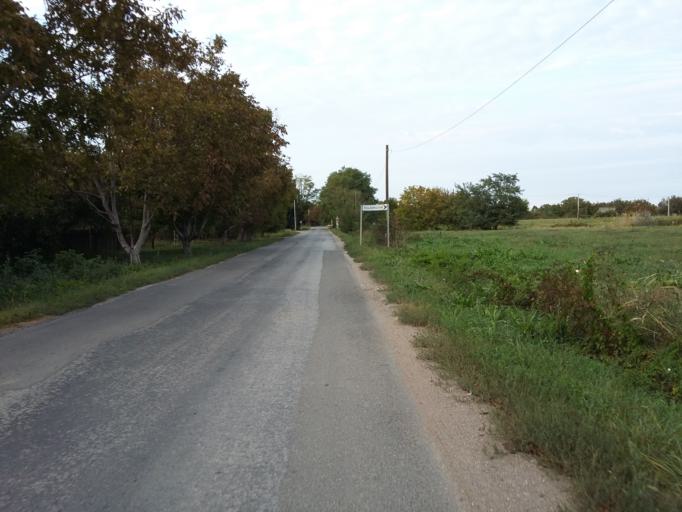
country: HU
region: Csongrad
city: Szeged
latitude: 46.2182
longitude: 20.1107
